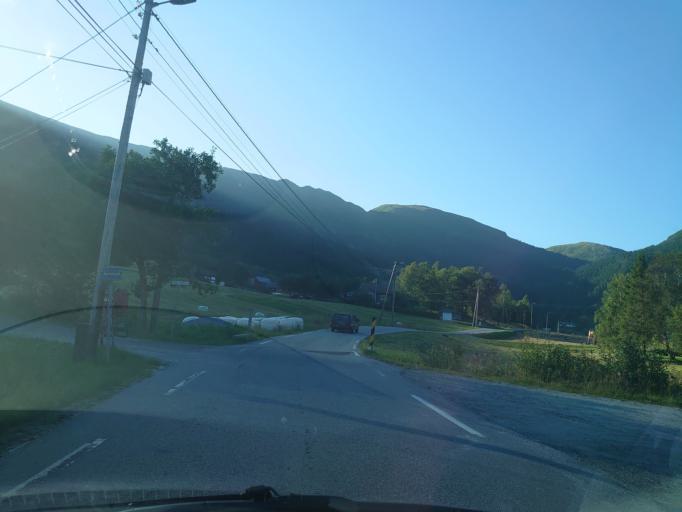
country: NO
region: Hordaland
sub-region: Bergen
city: Espeland
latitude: 60.3856
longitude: 5.4401
